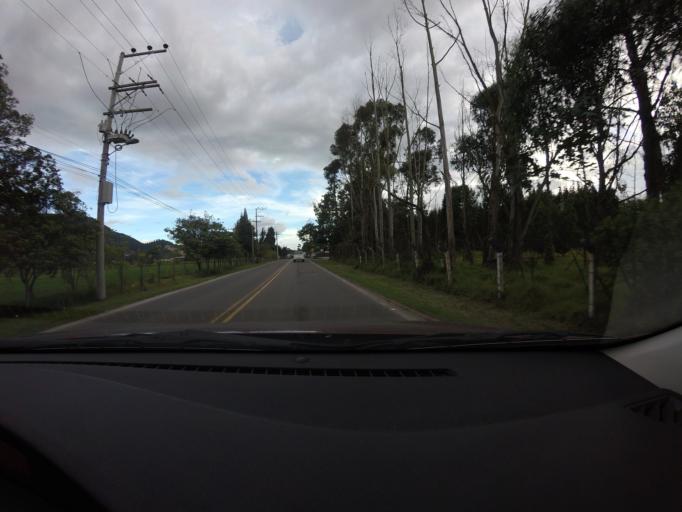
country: CO
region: Cundinamarca
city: Sopo
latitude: 4.9284
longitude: -73.9521
